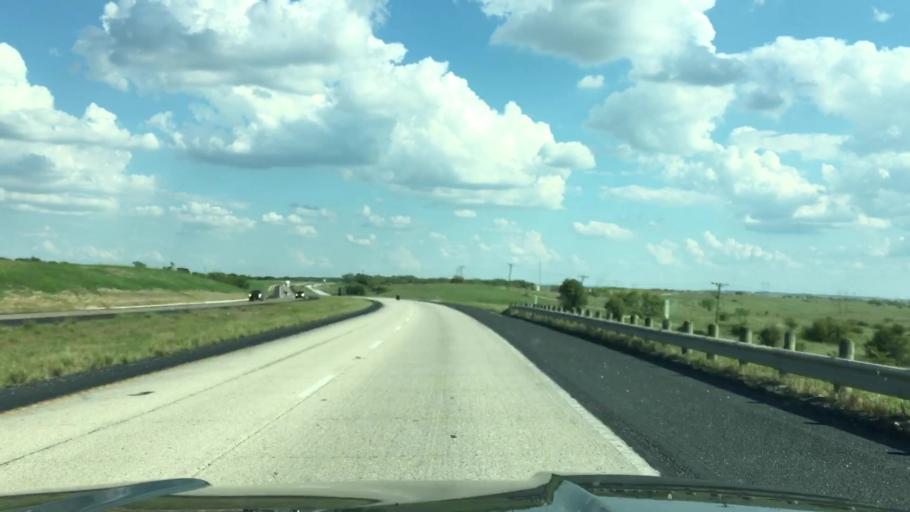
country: US
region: Texas
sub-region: Wise County
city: New Fairview
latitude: 33.1263
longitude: -97.4903
